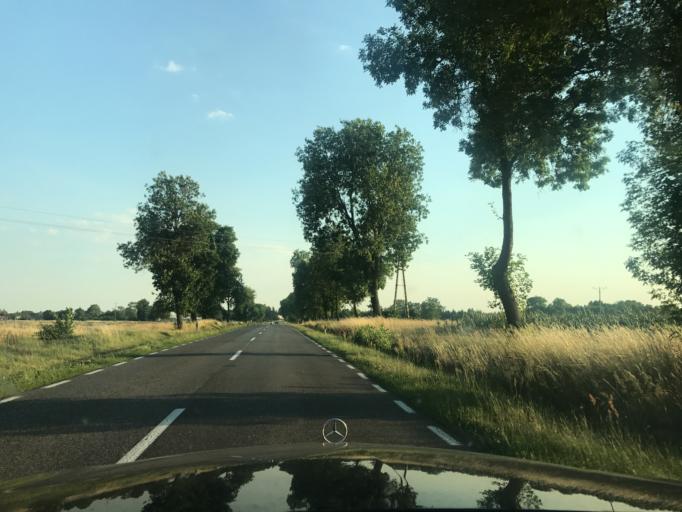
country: PL
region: Lublin Voivodeship
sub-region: Powiat parczewski
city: Debowa Kloda
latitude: 51.6580
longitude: 23.0026
